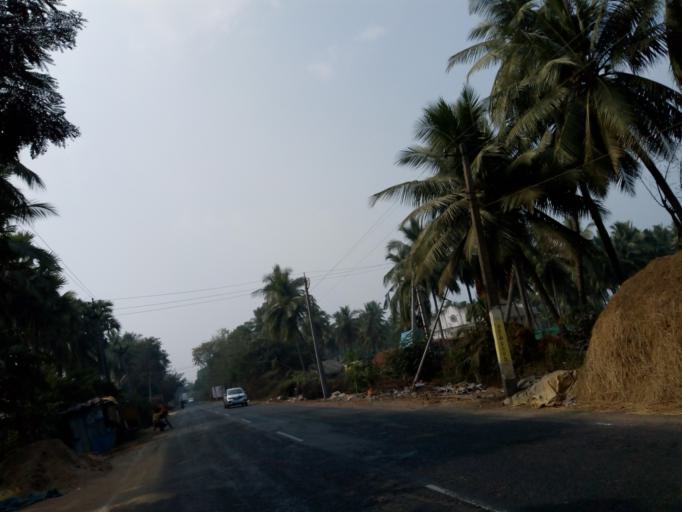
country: IN
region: Andhra Pradesh
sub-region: West Godavari
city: Akividu
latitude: 16.6297
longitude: 81.4658
